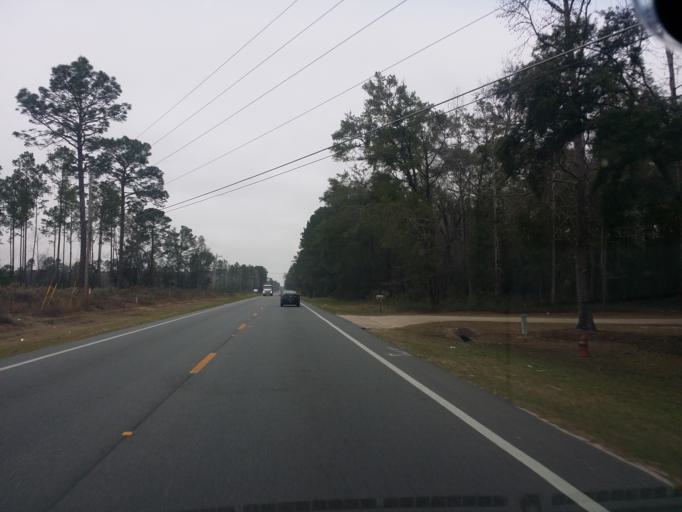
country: US
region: Florida
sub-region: Wakulla County
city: Crawfordville
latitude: 30.2293
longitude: -84.3623
